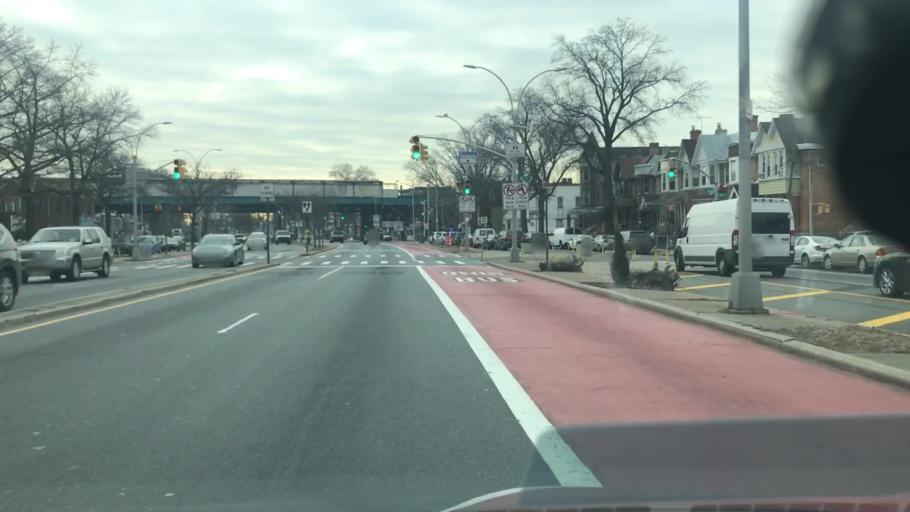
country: US
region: New York
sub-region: Queens County
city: Borough of Queens
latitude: 40.6952
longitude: -73.8527
